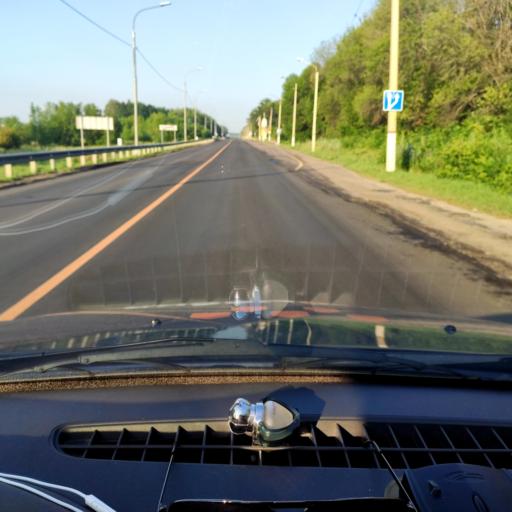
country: RU
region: Lipetsk
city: Izmalkovo
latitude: 52.4717
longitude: 38.0250
